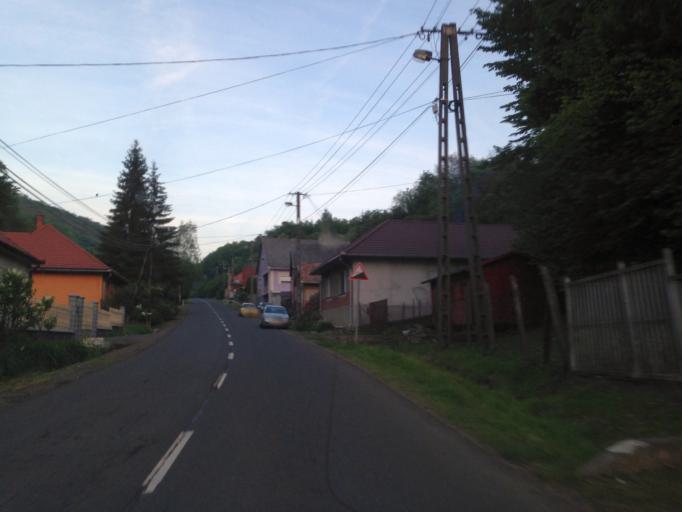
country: HU
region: Nograd
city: Batonyterenye
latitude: 47.9017
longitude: 19.8123
